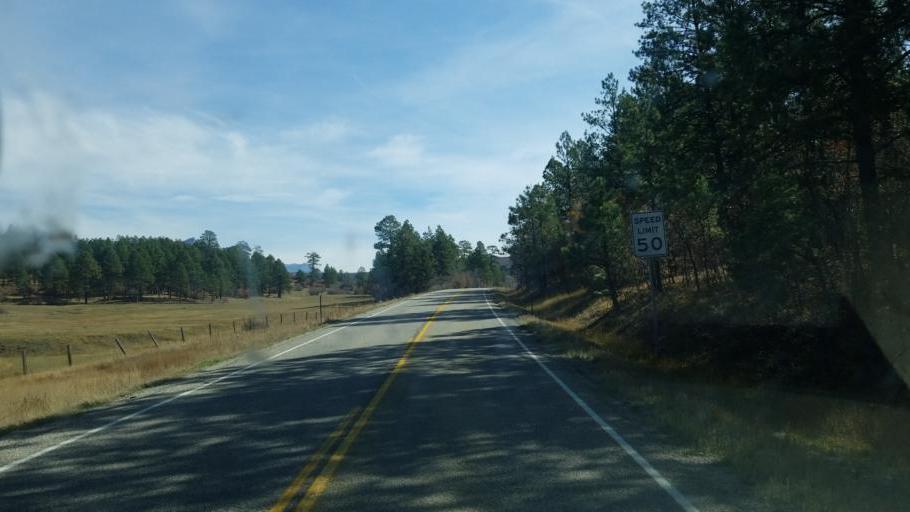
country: US
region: New Mexico
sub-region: Rio Arriba County
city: Dulce
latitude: 37.0749
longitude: -106.8386
